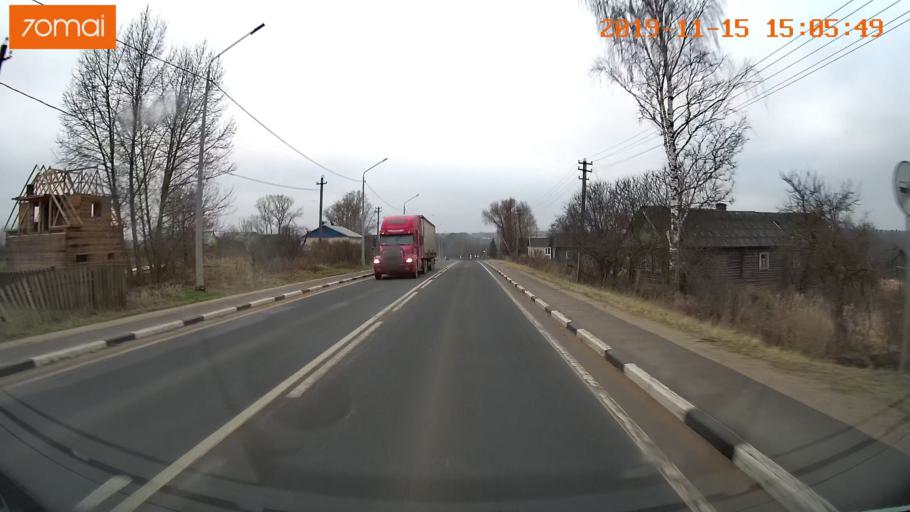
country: RU
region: Jaroslavl
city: Prechistoye
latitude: 58.3994
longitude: 40.3192
